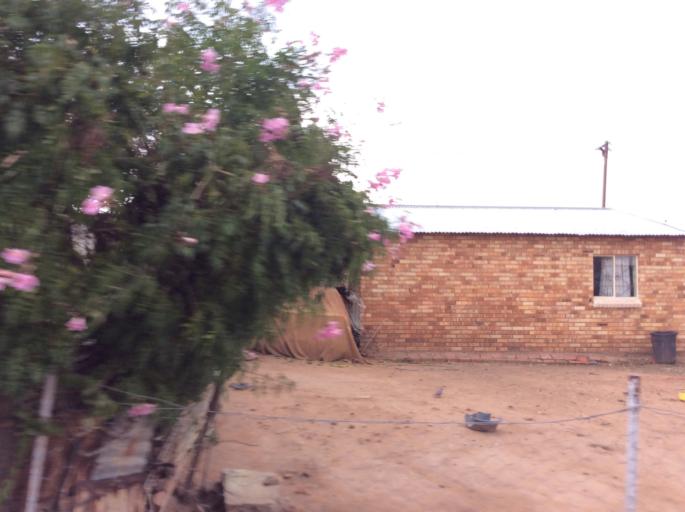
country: ZA
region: Orange Free State
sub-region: Xhariep District Municipality
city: Dewetsdorp
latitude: -29.5848
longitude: 26.6724
